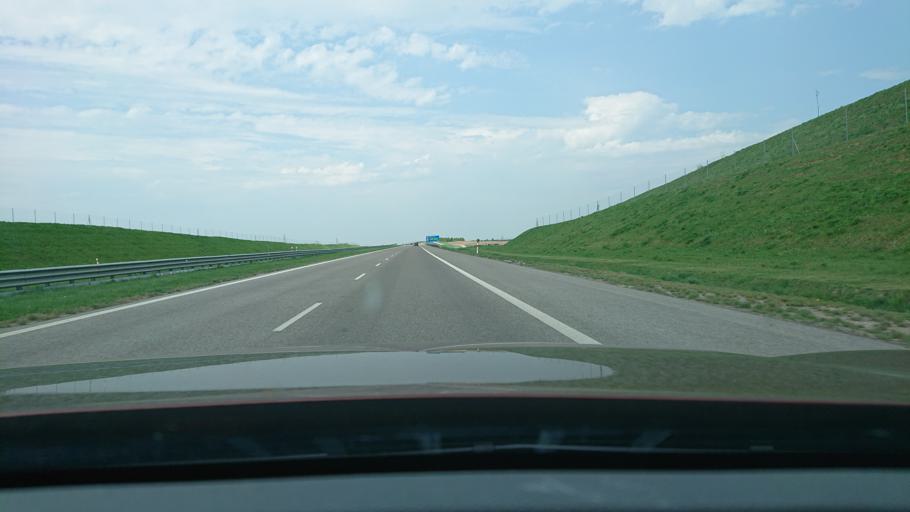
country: PL
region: Subcarpathian Voivodeship
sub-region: Powiat jaroslawski
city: Pawlosiow
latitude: 49.9541
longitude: 22.6617
